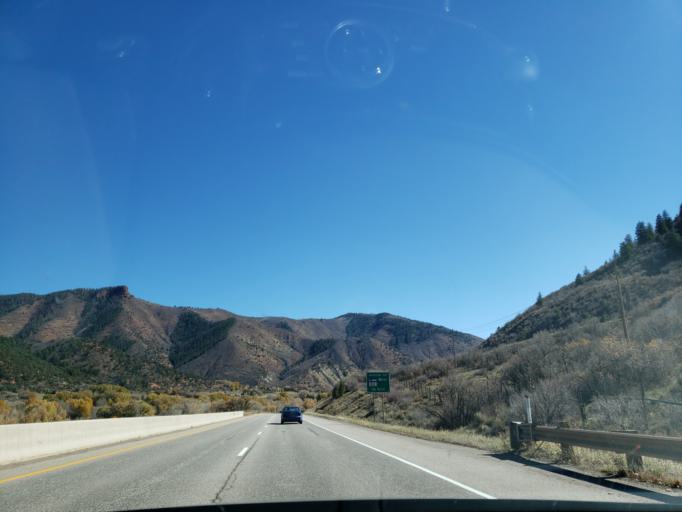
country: US
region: Colorado
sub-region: Eagle County
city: Basalt
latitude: 39.3265
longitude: -106.9564
